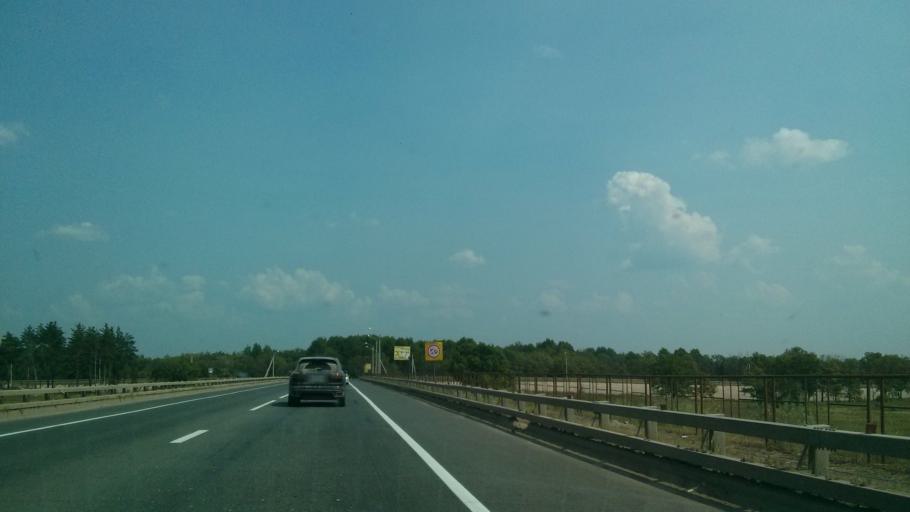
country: RU
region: Nizjnij Novgorod
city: Navashino
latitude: 55.5865
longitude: 42.1453
